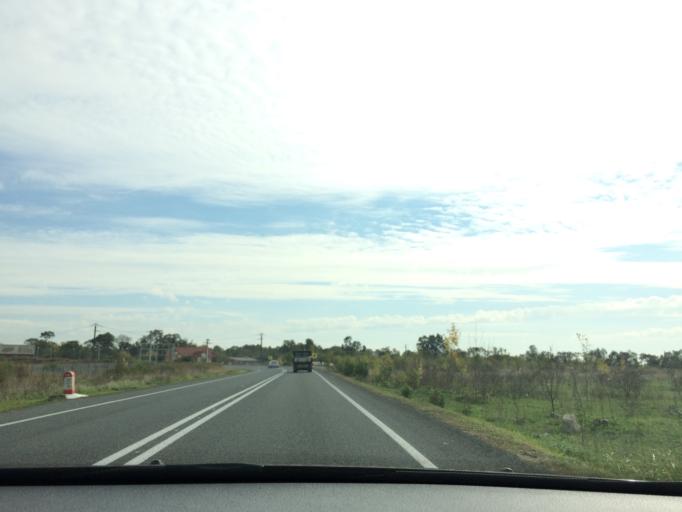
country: RO
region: Timis
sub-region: Comuna Remetea Mare
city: Remetea Mare
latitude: 45.7785
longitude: 21.3555
